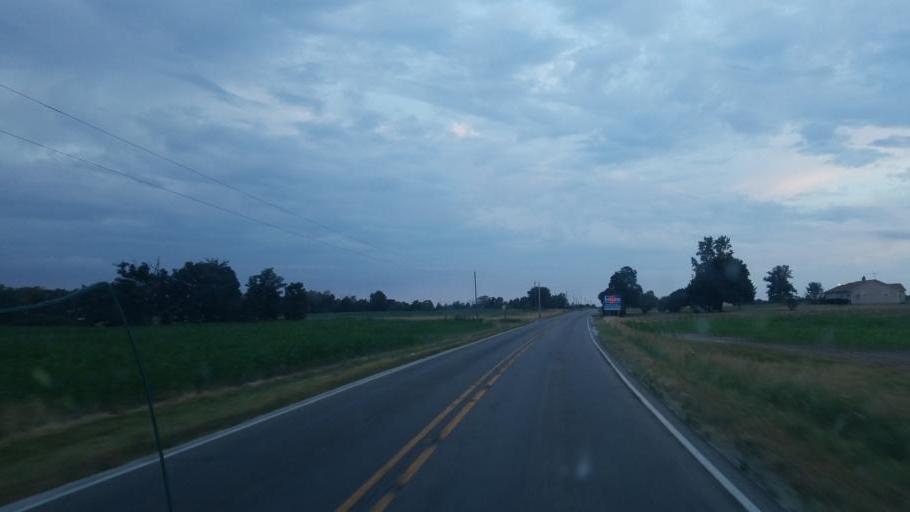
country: US
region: Ohio
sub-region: Defiance County
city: Hicksville
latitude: 41.3282
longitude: -84.8088
